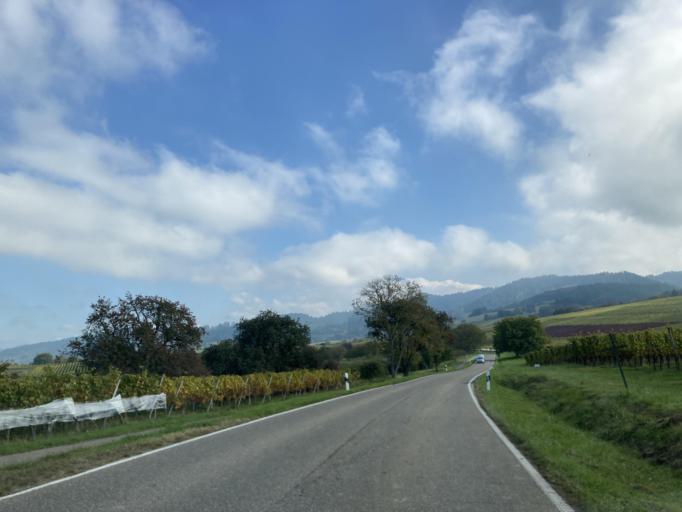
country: DE
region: Baden-Wuerttemberg
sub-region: Freiburg Region
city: Badenweiler
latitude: 47.8254
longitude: 7.6593
